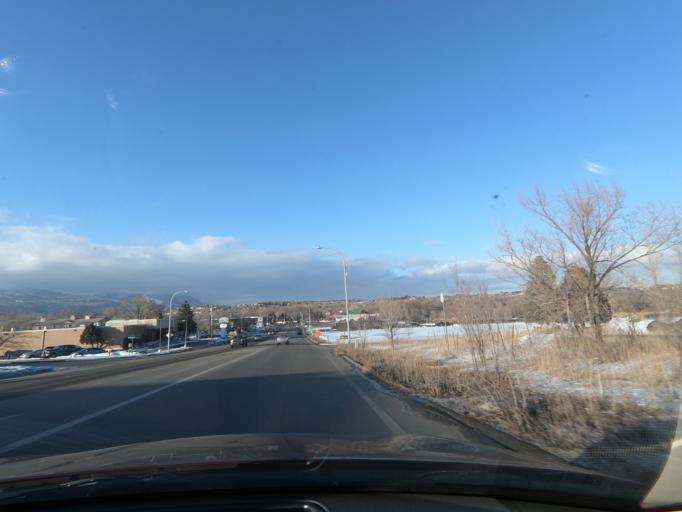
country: US
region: Colorado
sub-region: El Paso County
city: Colorado Springs
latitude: 38.8369
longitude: -104.8591
